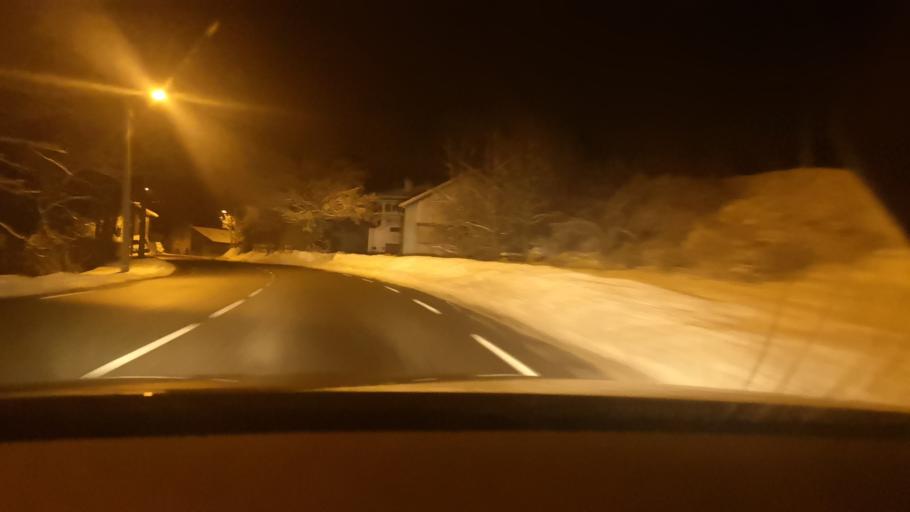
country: FR
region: Rhone-Alpes
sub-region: Departement de l'Ain
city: Chatillon-en-Michaille
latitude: 46.1712
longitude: 5.7246
